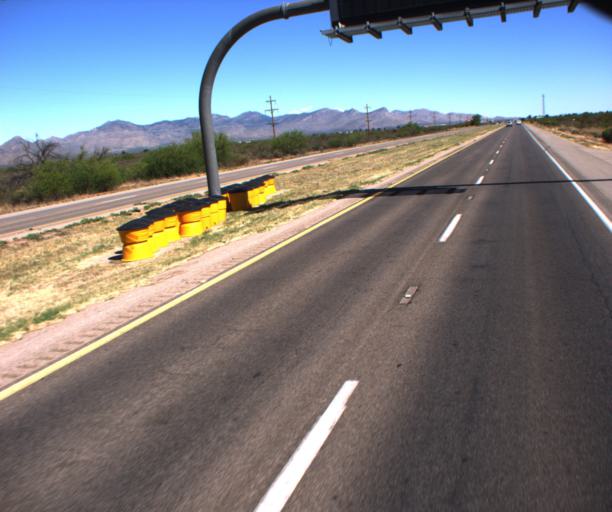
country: US
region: Arizona
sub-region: Cochise County
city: Huachuca City
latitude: 31.6702
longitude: -110.3502
